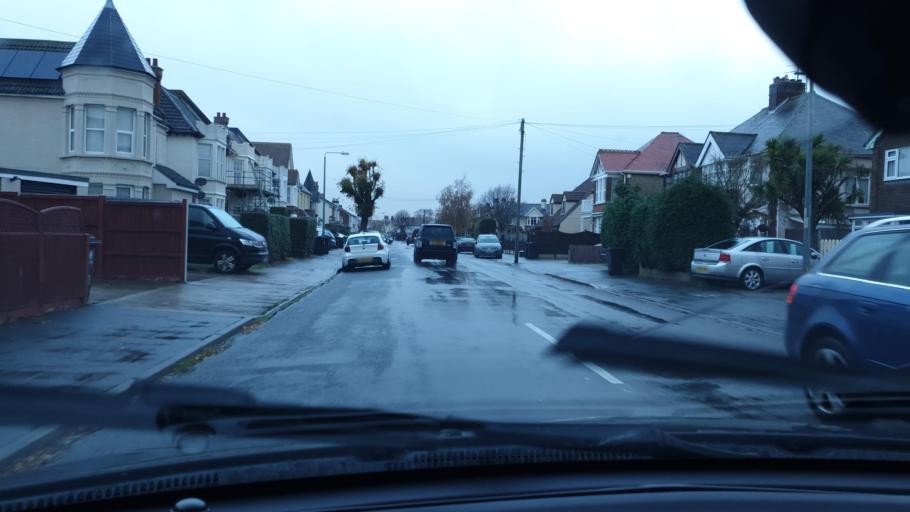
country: GB
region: England
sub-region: Essex
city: Clacton-on-Sea
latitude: 51.7942
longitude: 1.1599
